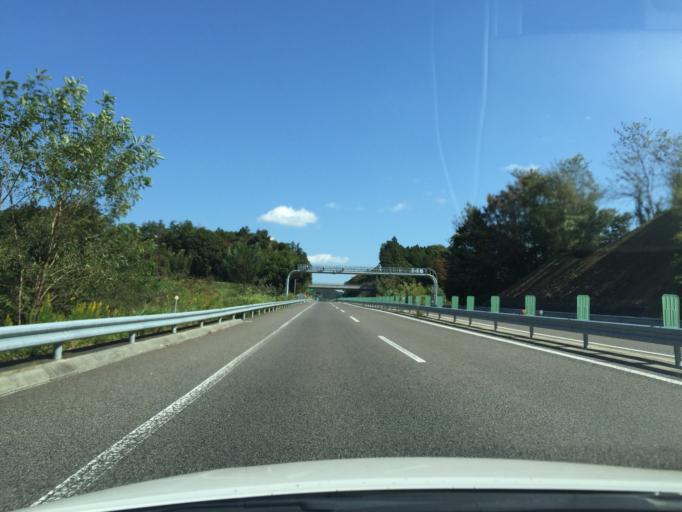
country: JP
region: Fukushima
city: Ishikawa
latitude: 37.2024
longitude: 140.4303
